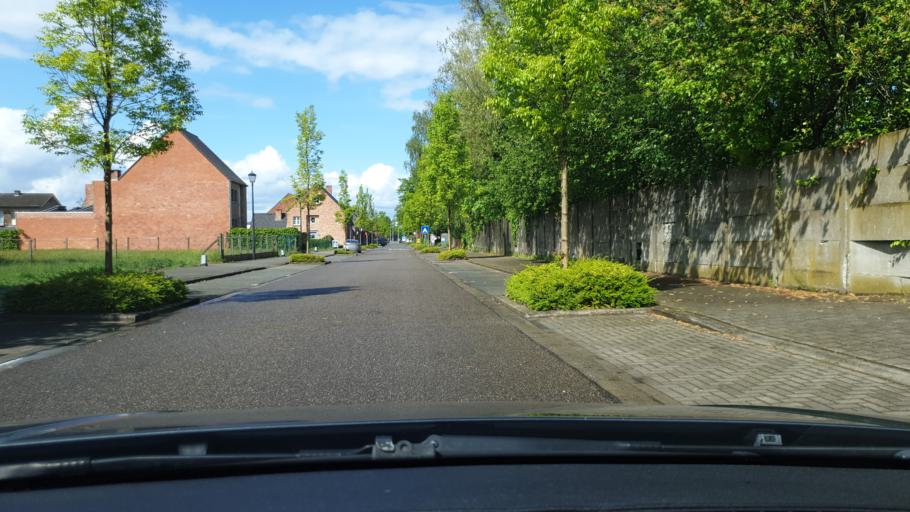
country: BE
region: Flanders
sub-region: Provincie Antwerpen
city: Geel
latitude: 51.2017
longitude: 4.9799
